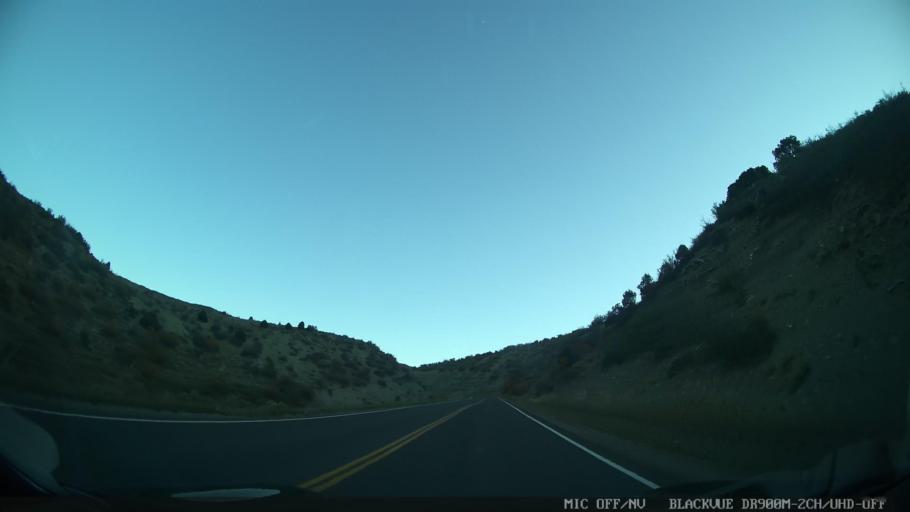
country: US
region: Colorado
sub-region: Eagle County
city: Edwards
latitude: 39.8044
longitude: -106.6781
